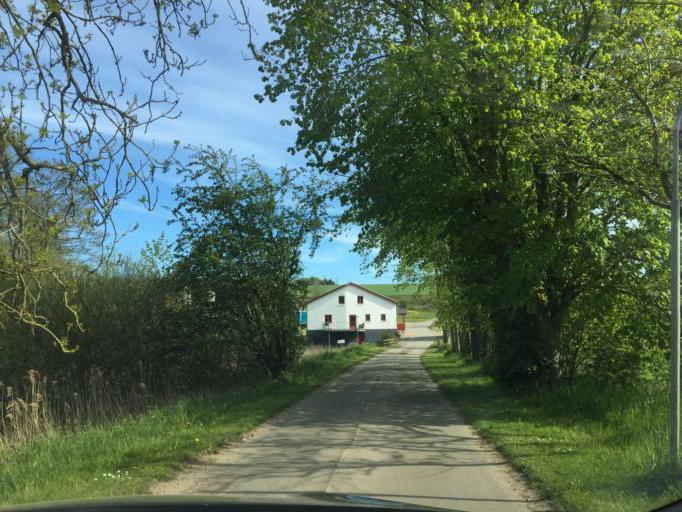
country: DK
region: South Denmark
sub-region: Fredericia Kommune
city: Taulov
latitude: 55.5347
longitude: 9.5643
